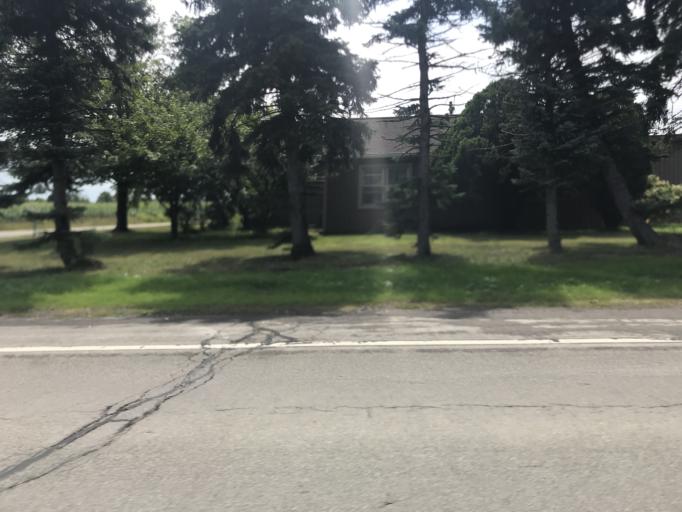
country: US
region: New York
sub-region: Chautauqua County
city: Dunkirk
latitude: 42.5093
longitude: -79.2823
